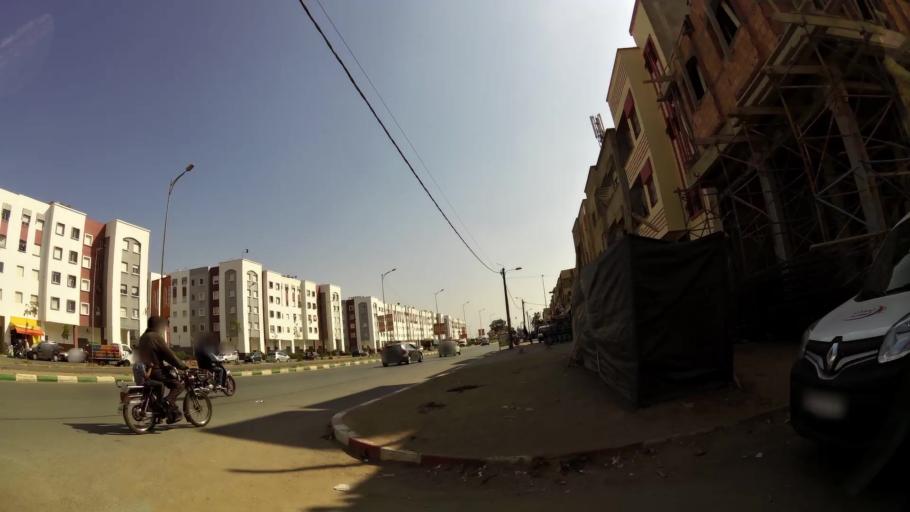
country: MA
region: Rabat-Sale-Zemmour-Zaer
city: Sale
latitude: 34.0648
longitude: -6.7639
